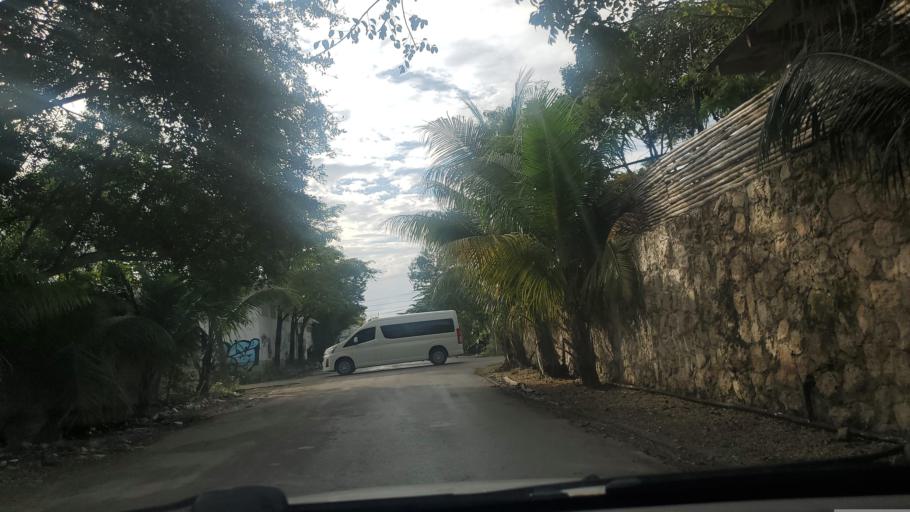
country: MX
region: Quintana Roo
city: Tulum
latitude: 20.2147
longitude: -87.4551
